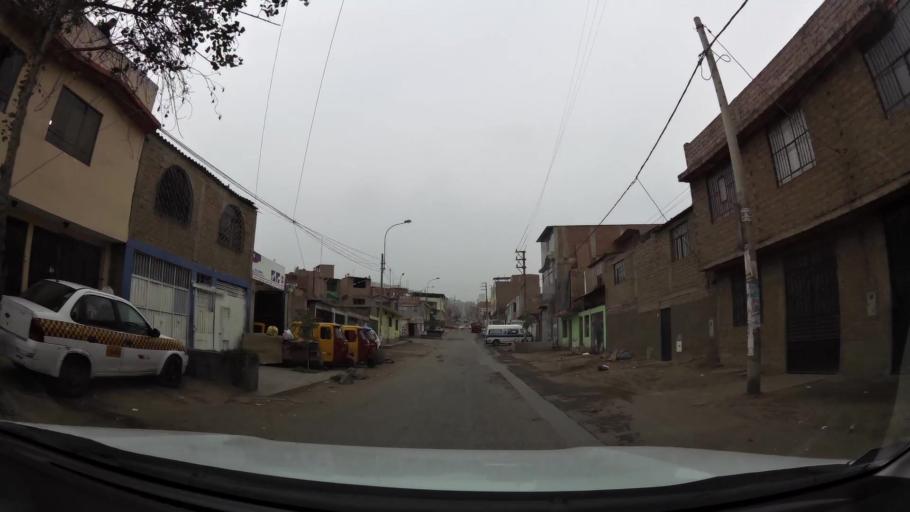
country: PE
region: Lima
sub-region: Lima
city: Surco
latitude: -12.1780
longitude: -76.9673
